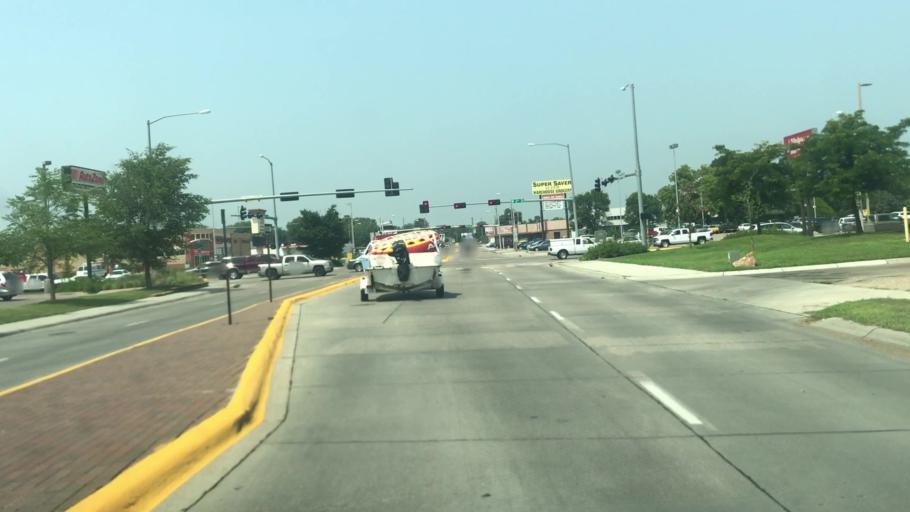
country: US
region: Nebraska
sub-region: Hall County
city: Grand Island
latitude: 40.9172
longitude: -98.3565
